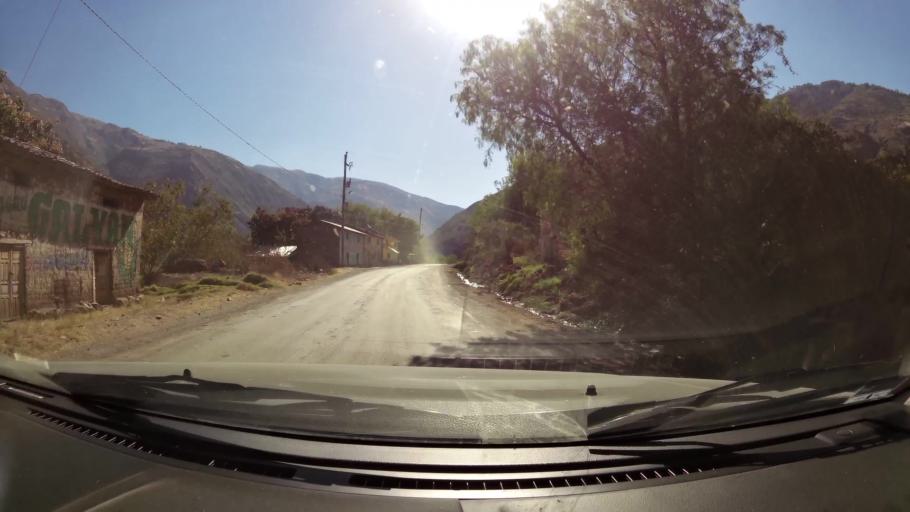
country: PE
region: Huancavelica
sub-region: Provincia de Acobamba
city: Pomacocha
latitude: -12.7677
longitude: -74.5060
